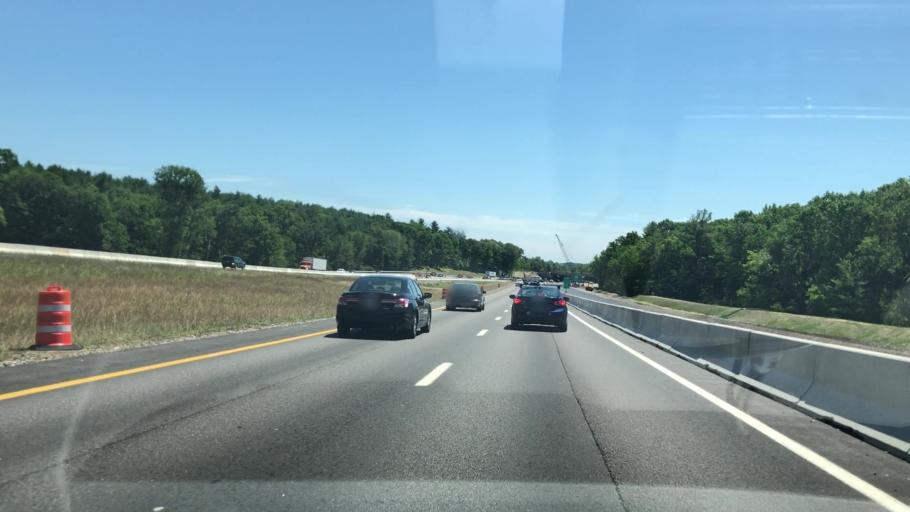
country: US
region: New Hampshire
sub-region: Rockingham County
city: Derry
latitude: 42.8858
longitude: -71.3496
